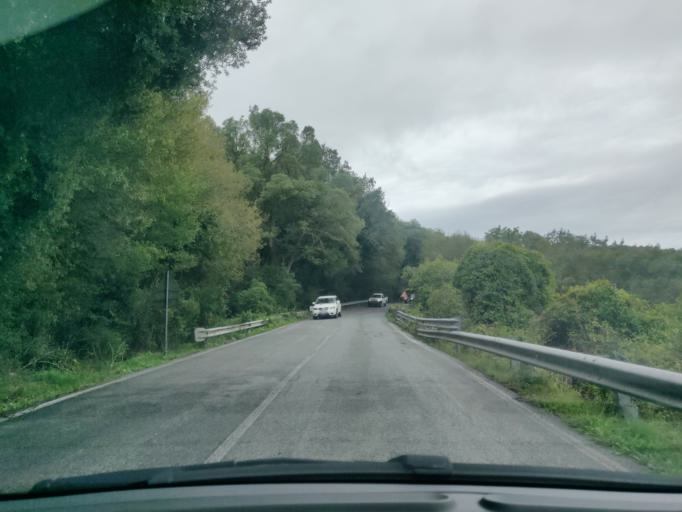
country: IT
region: Latium
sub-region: Citta metropolitana di Roma Capitale
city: Allumiere
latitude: 42.1398
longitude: 11.8738
